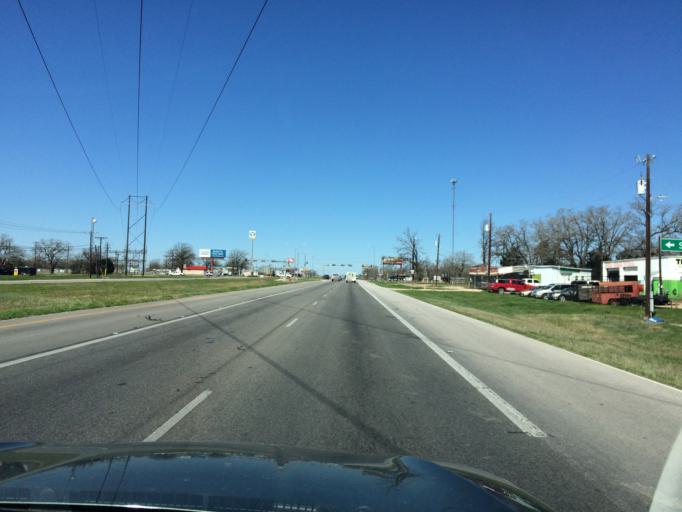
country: US
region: Texas
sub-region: Bastrop County
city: Wyldwood
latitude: 30.1212
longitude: -97.4305
